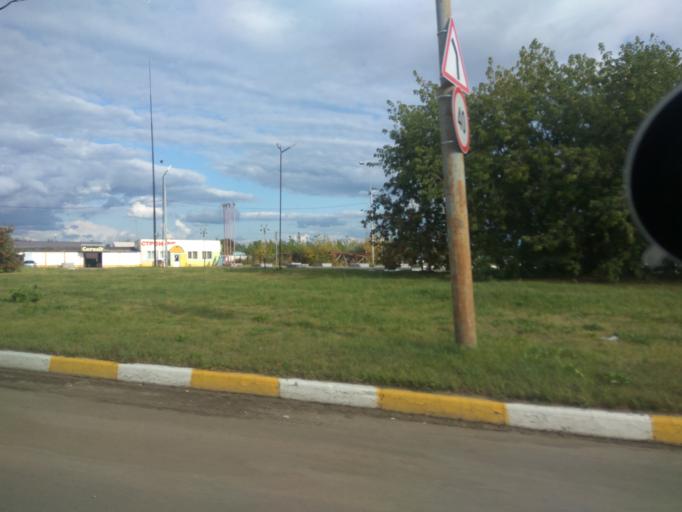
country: RU
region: Moskovskaya
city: Ramenskoye
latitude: 55.5607
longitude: 38.2626
